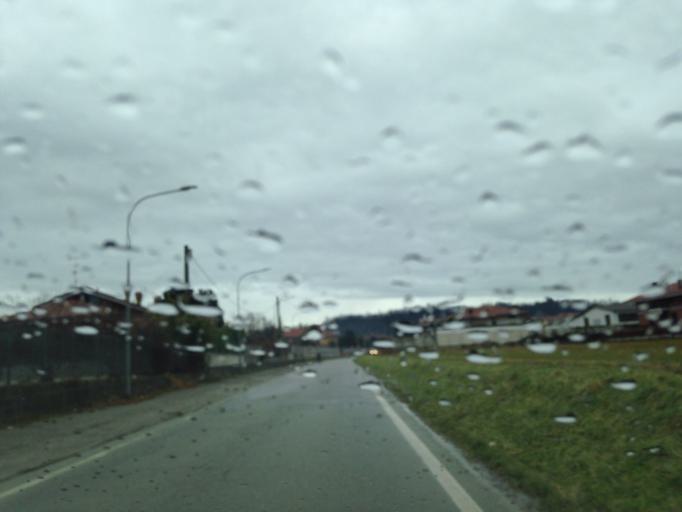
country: IT
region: Piedmont
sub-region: Provincia di Torino
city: Villareggia
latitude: 45.3056
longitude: 7.9778
